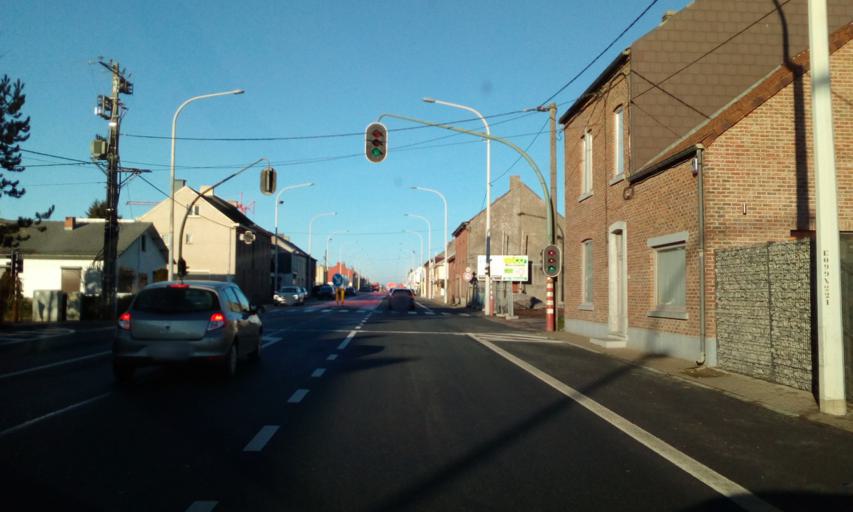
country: BE
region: Wallonia
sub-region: Province du Hainaut
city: Gerpinnes
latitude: 50.3374
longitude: 4.4745
